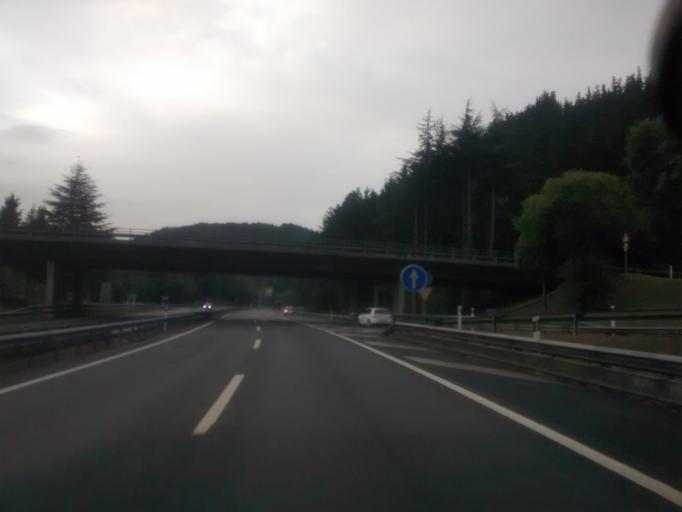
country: ES
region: Basque Country
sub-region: Provincia de Guipuzcoa
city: Elgoibar
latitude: 43.2321
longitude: -2.4046
